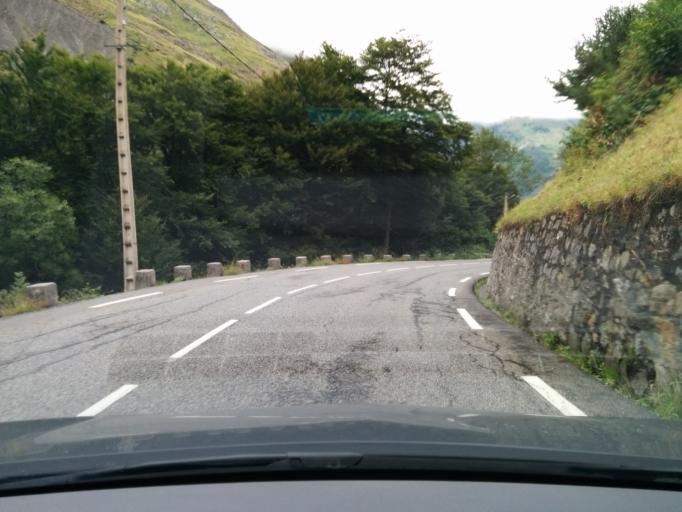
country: FR
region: Midi-Pyrenees
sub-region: Departement des Hautes-Pyrenees
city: Saint-Lary-Soulan
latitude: 42.7811
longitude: 0.1991
